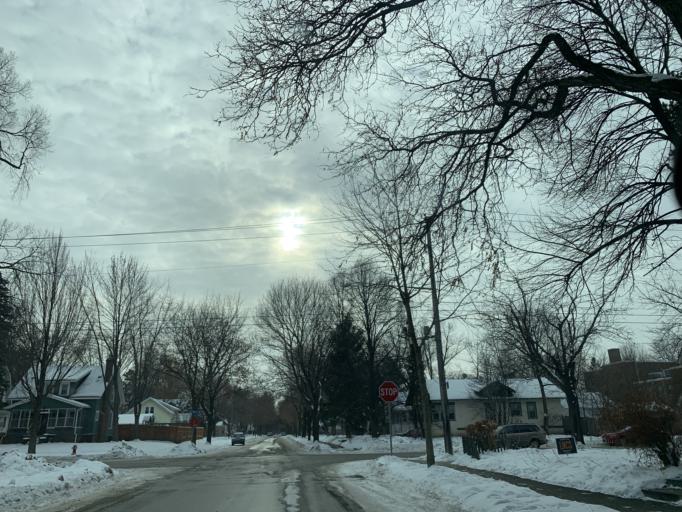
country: US
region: Minnesota
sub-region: Hennepin County
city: Richfield
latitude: 44.9130
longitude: -93.2178
